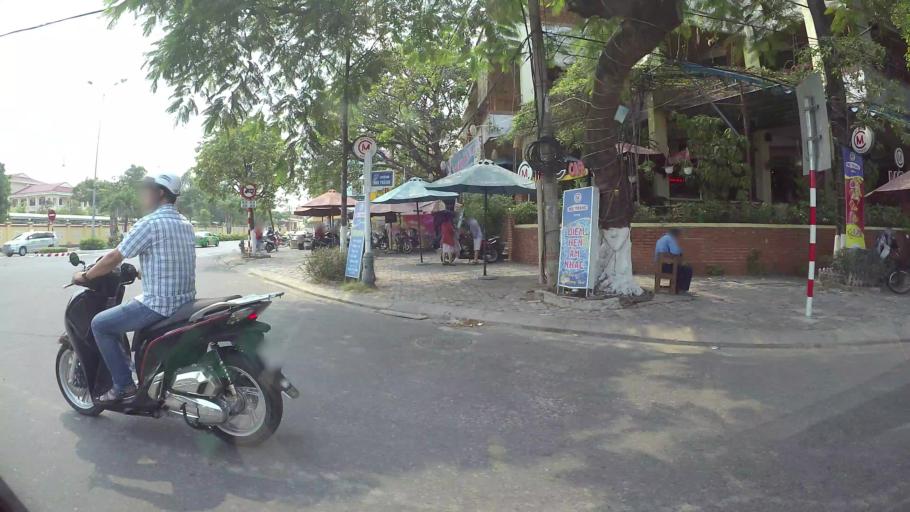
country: VN
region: Da Nang
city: Son Tra
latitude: 16.0497
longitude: 108.2205
